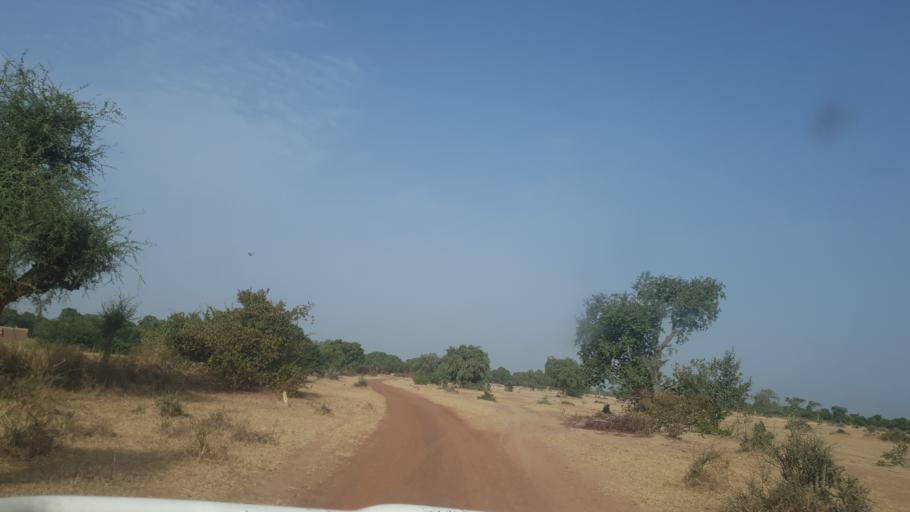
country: ML
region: Segou
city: Baroueli
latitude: 13.3570
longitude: -6.9252
